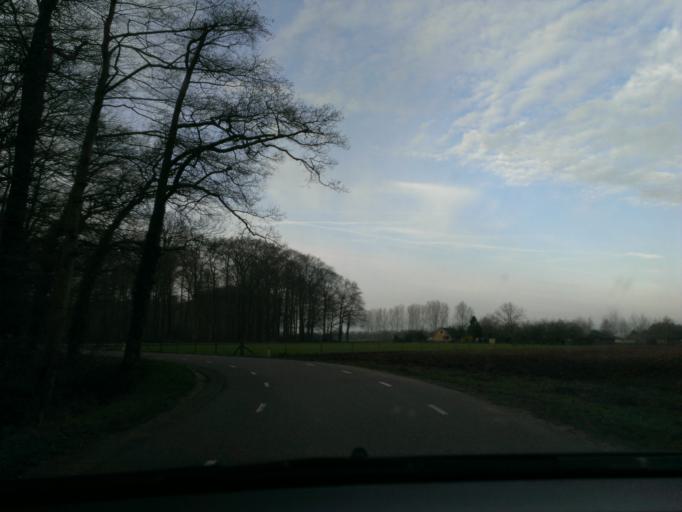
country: NL
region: Gelderland
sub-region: Gemeente Voorst
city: Twello
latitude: 52.2226
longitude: 6.1073
